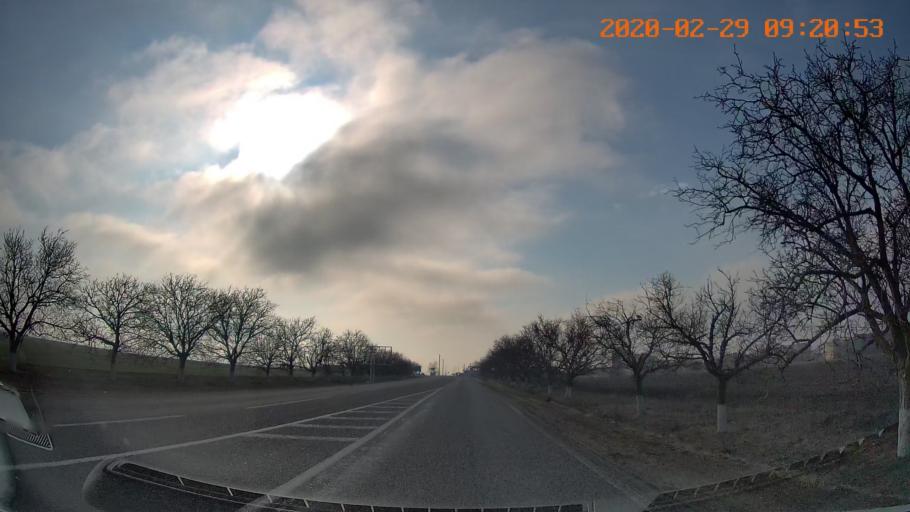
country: MD
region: Telenesti
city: Pervomaisc
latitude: 46.7428
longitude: 29.9532
